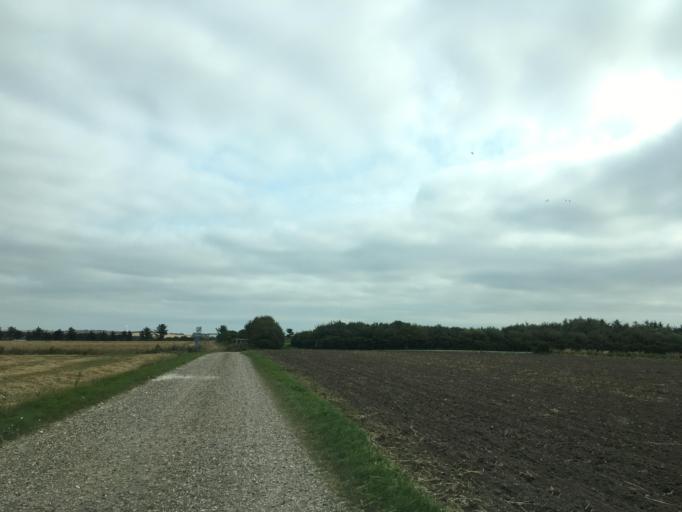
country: DK
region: Central Jutland
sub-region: Lemvig Kommune
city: Thyboron
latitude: 56.7883
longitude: 8.2833
